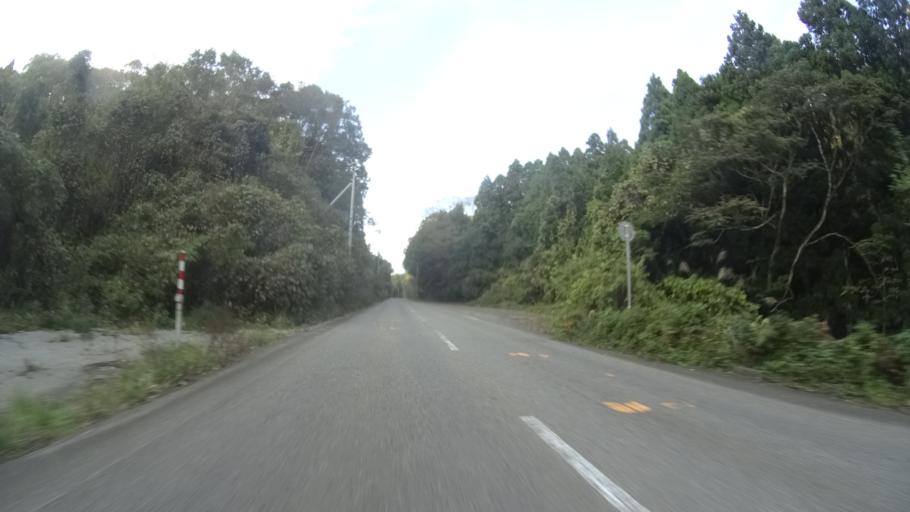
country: JP
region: Ishikawa
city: Nanao
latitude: 37.2013
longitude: 136.7081
